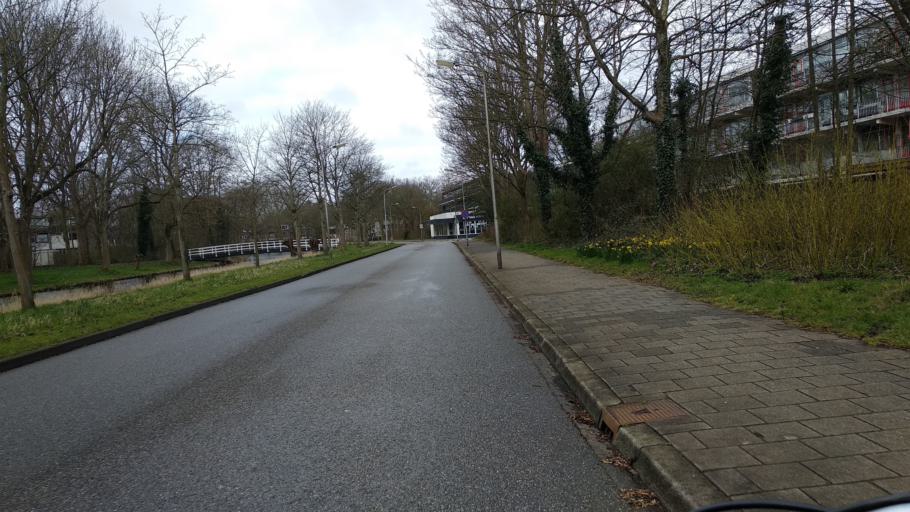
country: NL
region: South Holland
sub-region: Gemeente Delft
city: Delft
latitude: 51.9898
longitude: 4.3411
